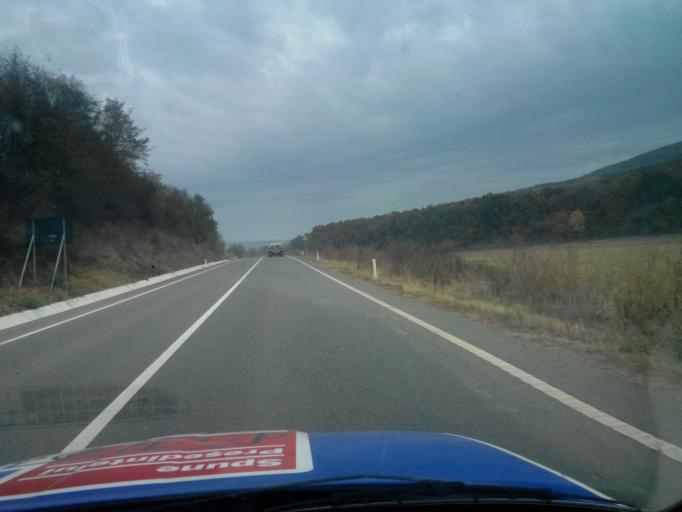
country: RO
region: Vaslui
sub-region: Comuna Tatarani
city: Tatarani
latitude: 46.6604
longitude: 27.9855
